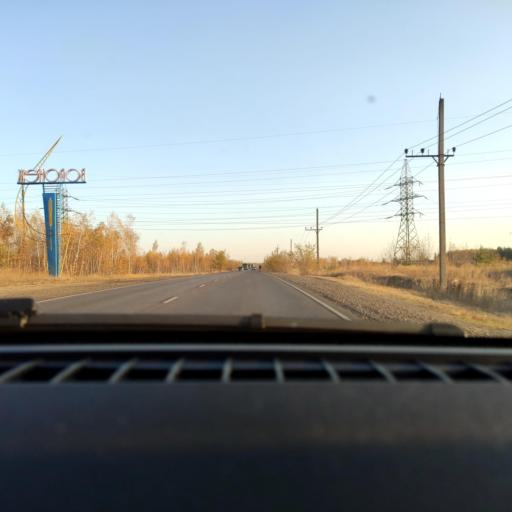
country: RU
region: Voronezj
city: Maslovka
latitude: 51.5818
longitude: 39.2610
